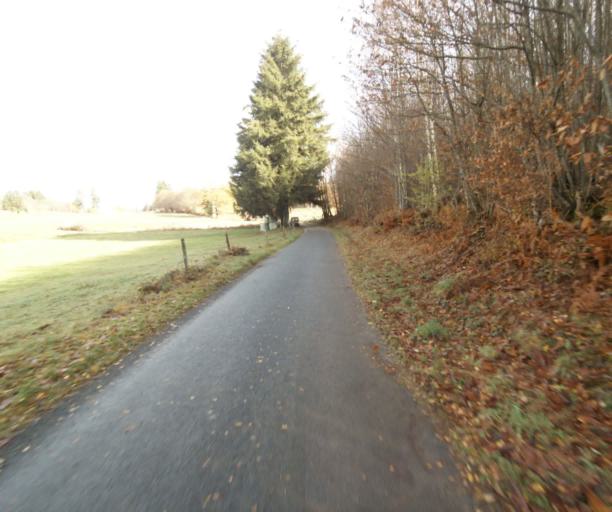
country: FR
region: Limousin
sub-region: Departement de la Correze
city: Sainte-Fortunade
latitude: 45.1961
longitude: 1.7452
